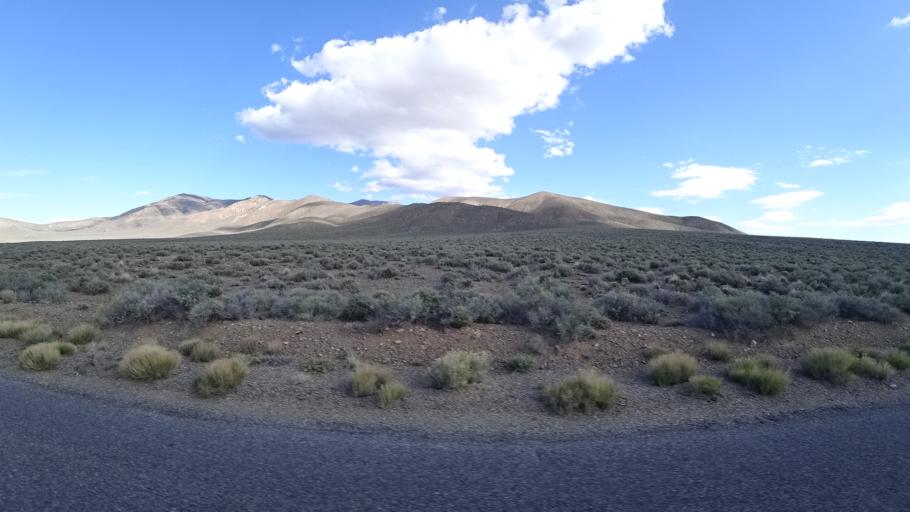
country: US
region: California
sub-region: San Bernardino County
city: Searles Valley
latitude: 36.3344
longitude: -117.1429
